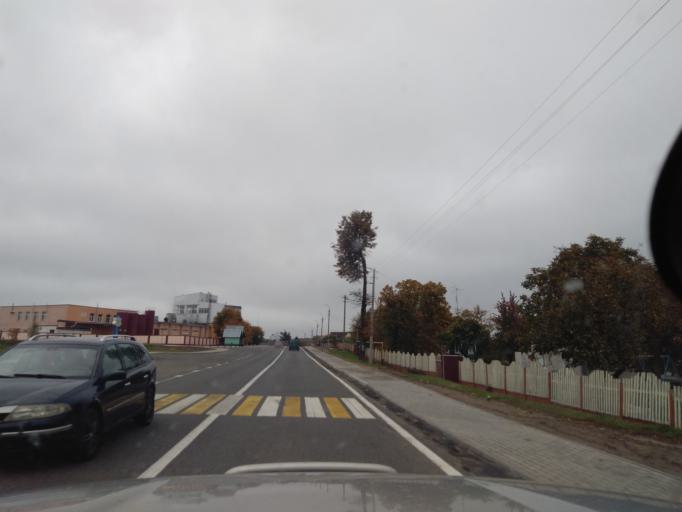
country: BY
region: Minsk
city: Kapyl'
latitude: 53.1408
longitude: 27.0897
